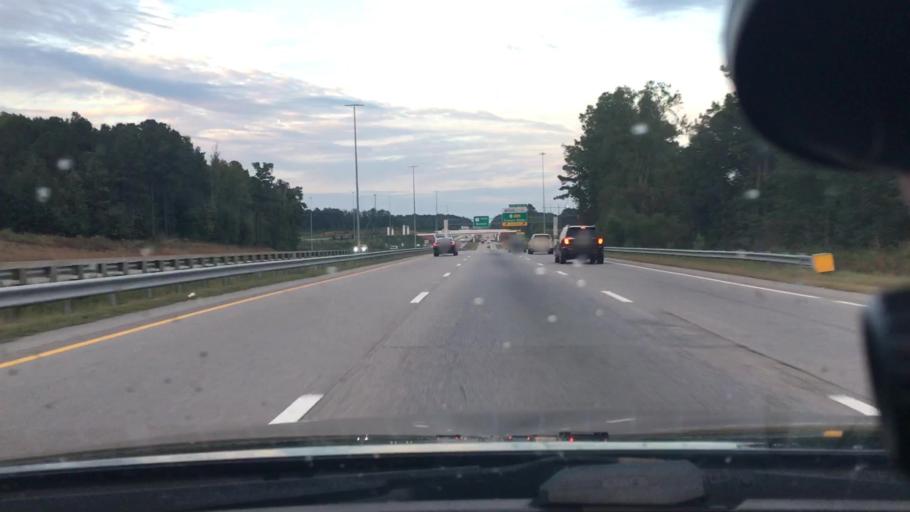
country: US
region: North Carolina
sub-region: Wake County
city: Apex
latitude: 35.6936
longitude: -78.8786
